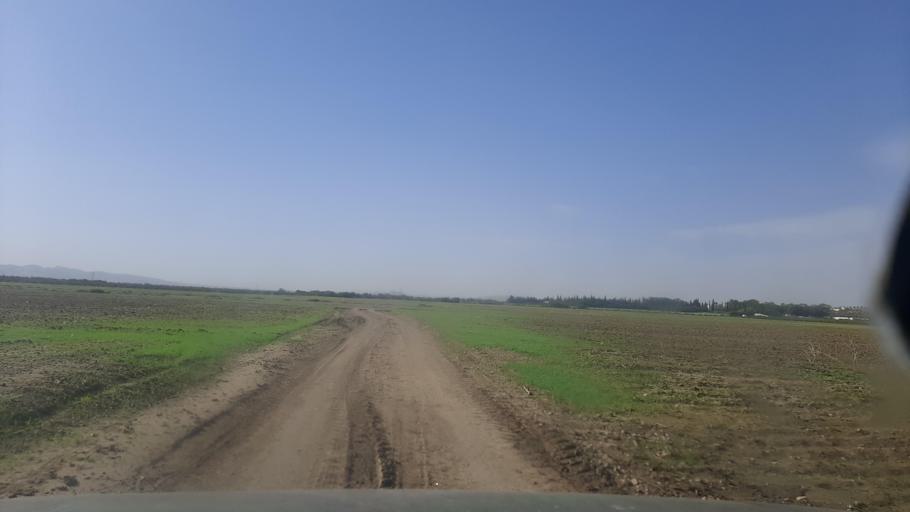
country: TN
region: Tunis
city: La Mohammedia
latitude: 36.6433
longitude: 10.0910
